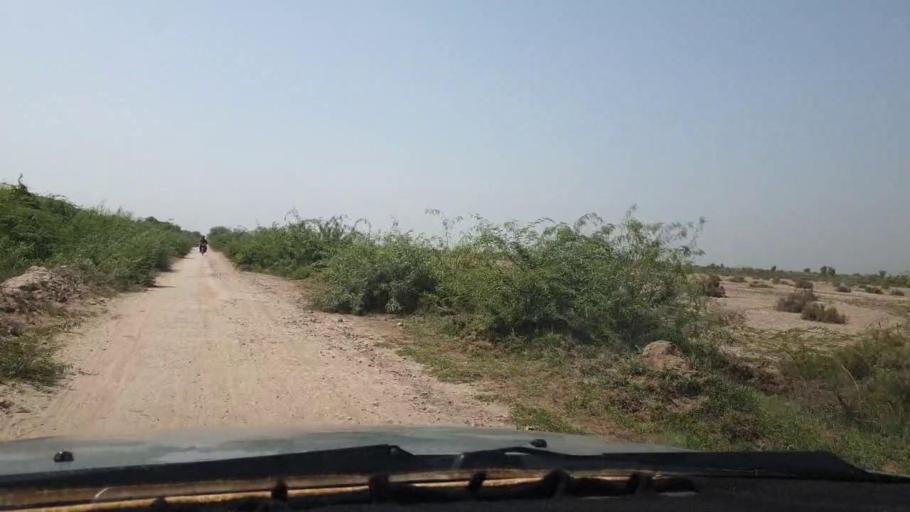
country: PK
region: Sindh
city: Tando Ghulam Ali
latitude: 25.1431
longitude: 68.8097
